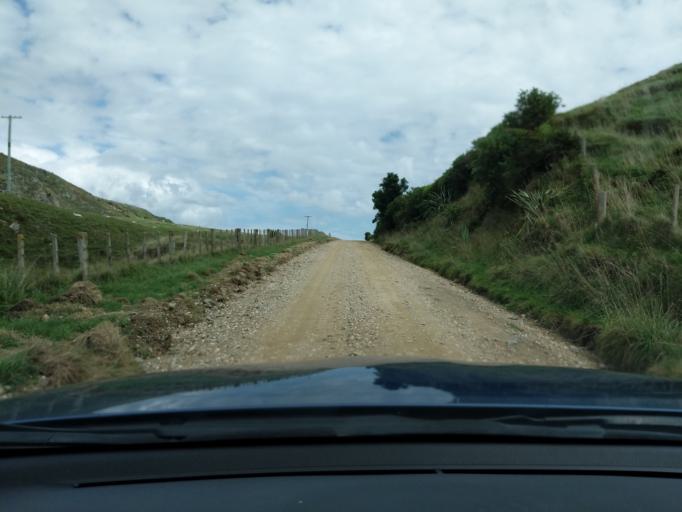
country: NZ
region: Tasman
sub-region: Tasman District
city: Takaka
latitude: -40.6472
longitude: 172.4289
